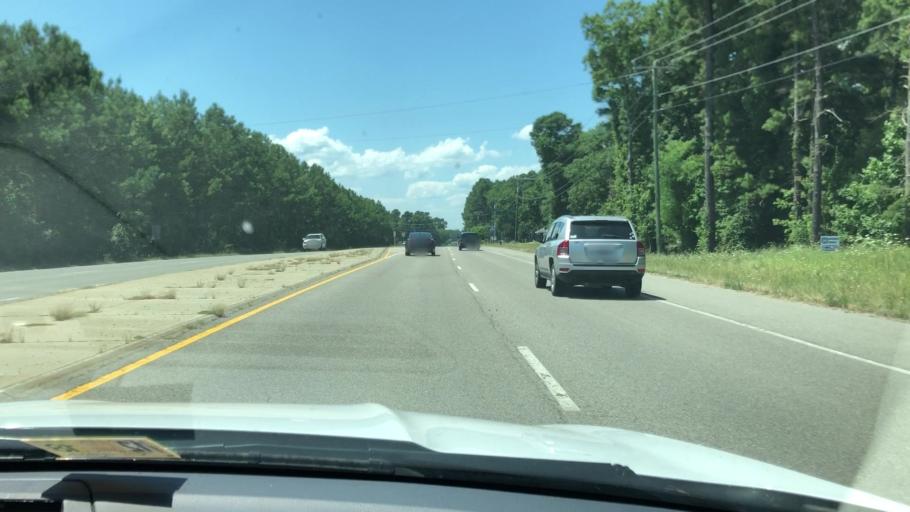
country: US
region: Virginia
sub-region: Middlesex County
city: Saluda
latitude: 37.5956
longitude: -76.5047
